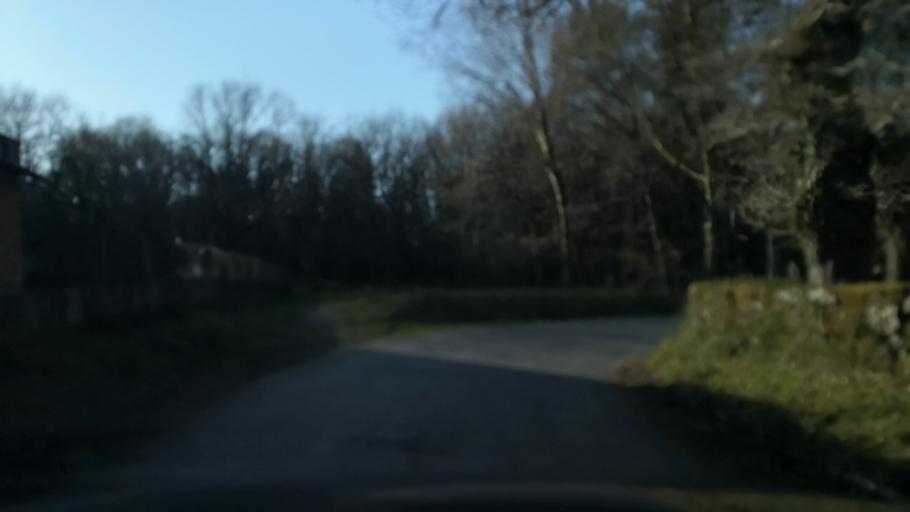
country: ES
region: Galicia
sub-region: Provincia de Lugo
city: Corgo
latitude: 42.9345
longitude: -7.4469
